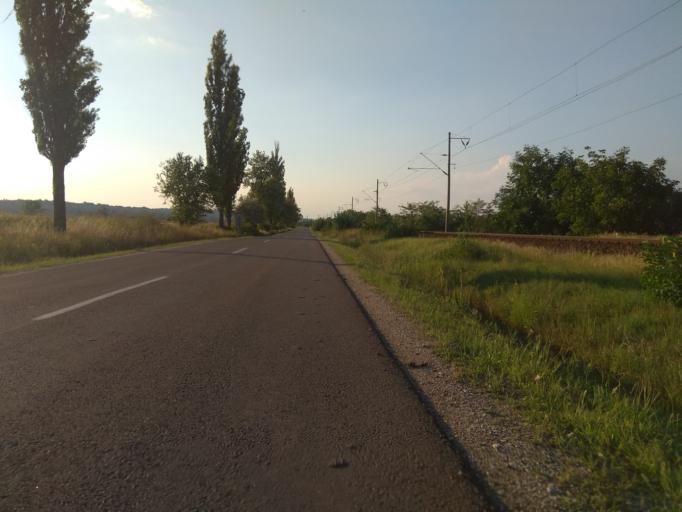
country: HU
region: Borsod-Abauj-Zemplen
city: Nyekladhaza
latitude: 47.9811
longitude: 20.8439
